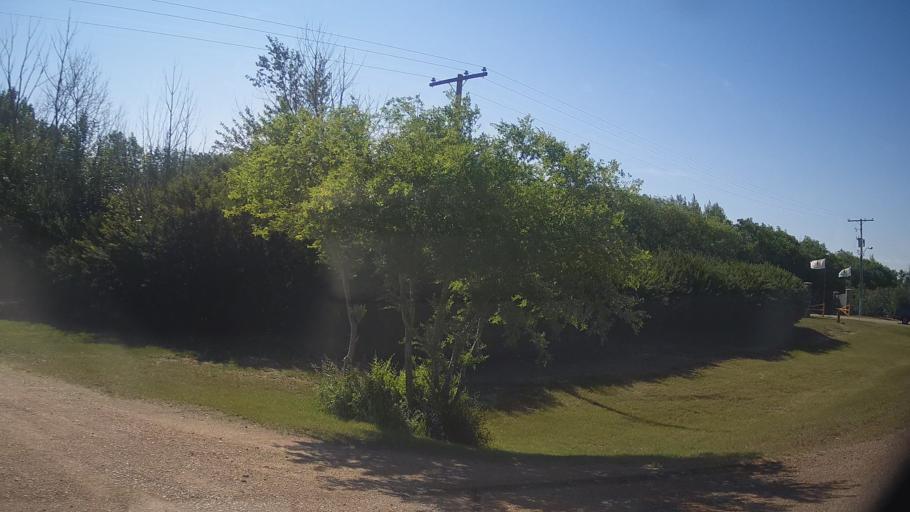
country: CA
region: Saskatchewan
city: Watrous
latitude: 51.7165
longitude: -105.4516
